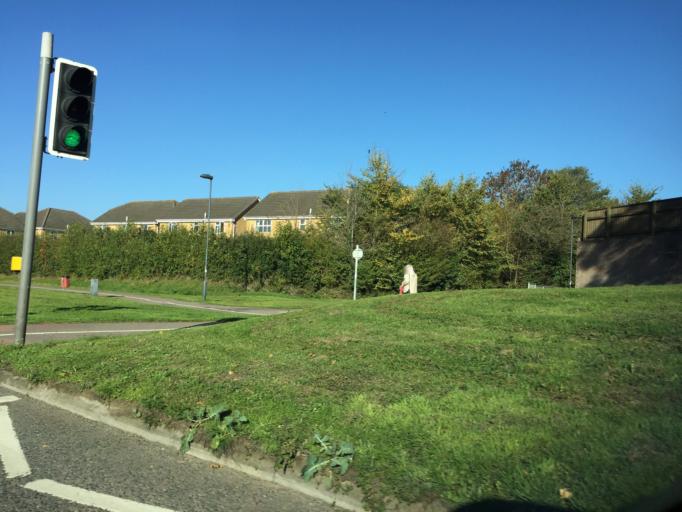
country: GB
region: England
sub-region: South Gloucestershire
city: Yate
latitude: 51.5497
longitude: -2.4107
